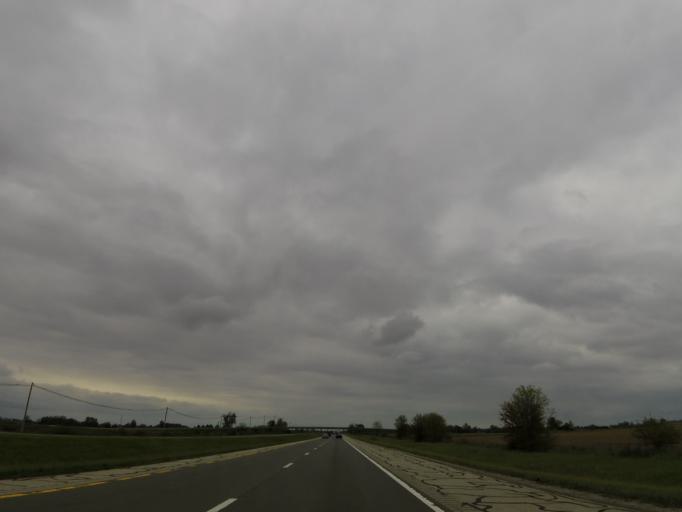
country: US
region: Ohio
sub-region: Fayette County
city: Jeffersonville
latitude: 39.6804
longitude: -83.4867
